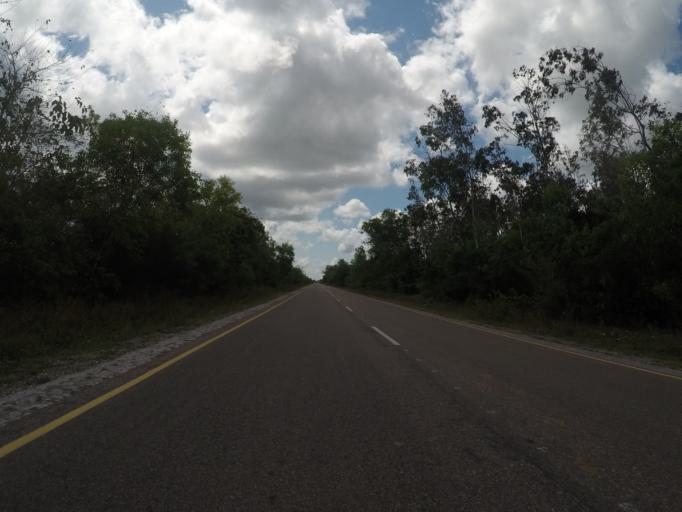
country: TZ
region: Zanzibar Central/South
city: Koani
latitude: -6.2602
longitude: 39.3588
